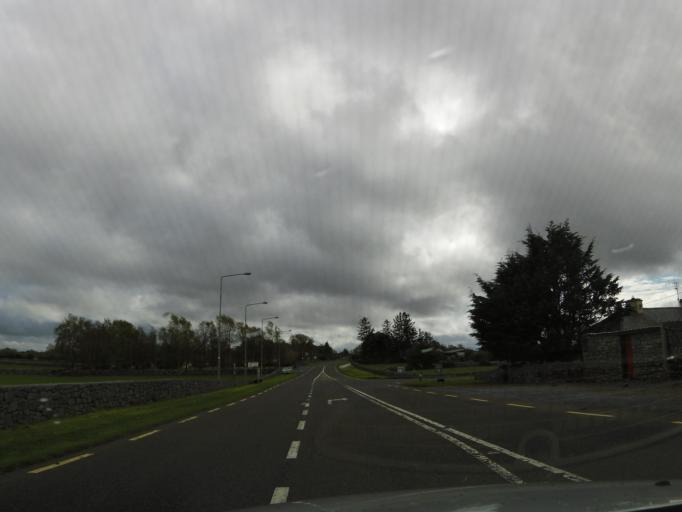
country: IE
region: Connaught
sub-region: Maigh Eo
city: Ballinrobe
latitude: 53.5684
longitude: -9.2326
